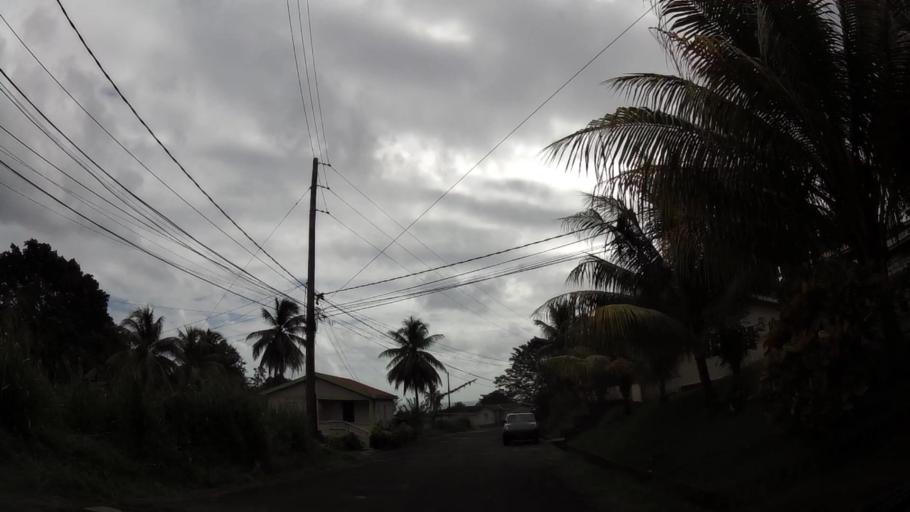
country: DM
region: Saint David
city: Castle Bruce
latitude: 15.4409
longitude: -61.2563
